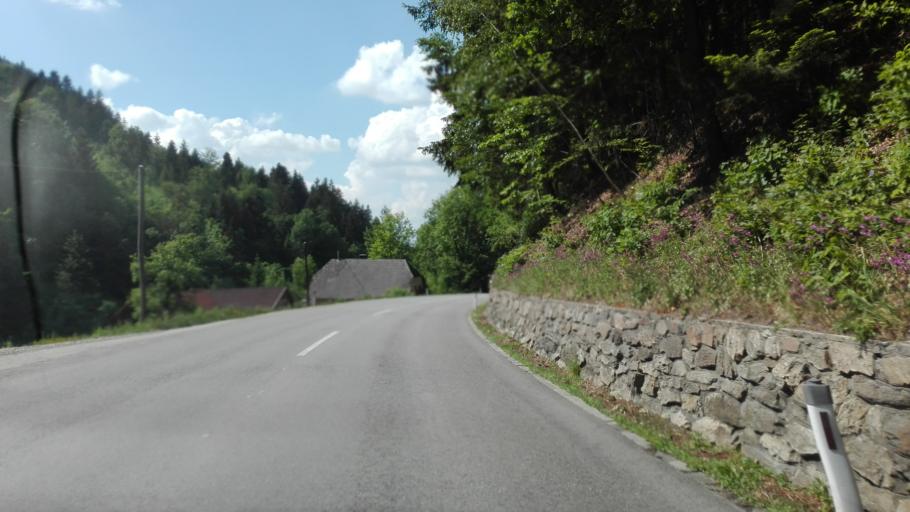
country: AT
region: Upper Austria
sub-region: Politischer Bezirk Rohrbach
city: Atzesberg
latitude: 48.4047
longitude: 13.8937
